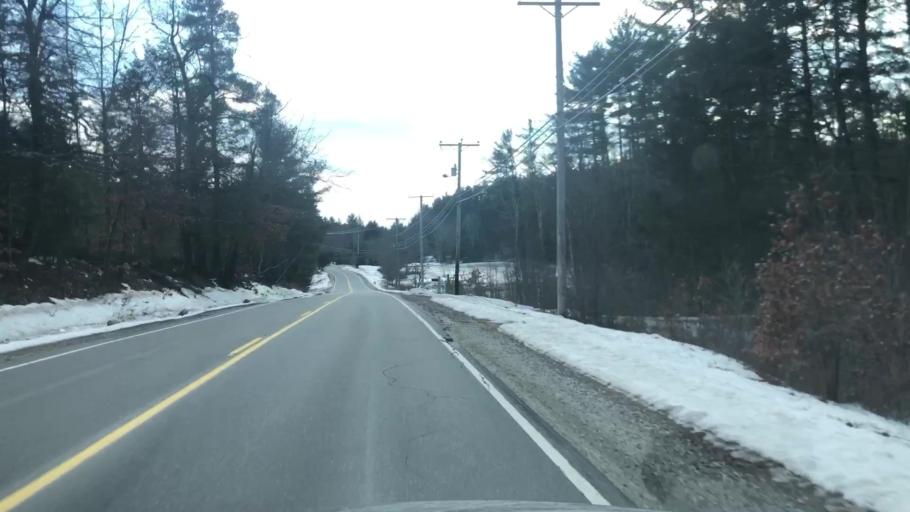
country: US
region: New Hampshire
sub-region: Hillsborough County
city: Mont Vernon
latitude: 42.8654
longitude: -71.6689
